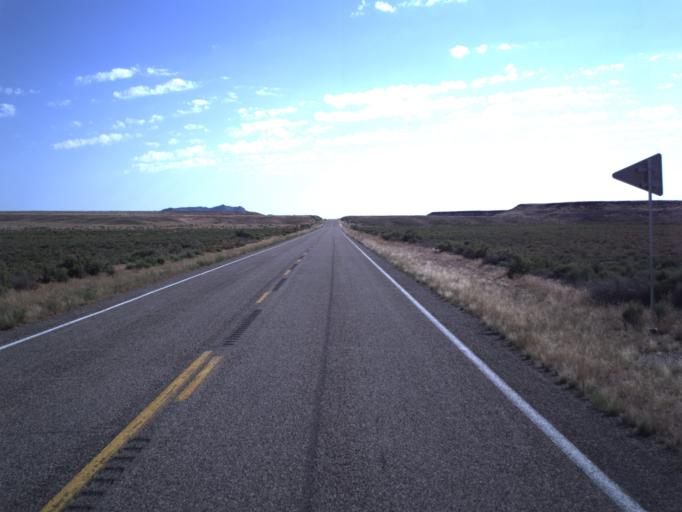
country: US
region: Utah
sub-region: Beaver County
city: Milford
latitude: 38.7367
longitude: -112.9628
